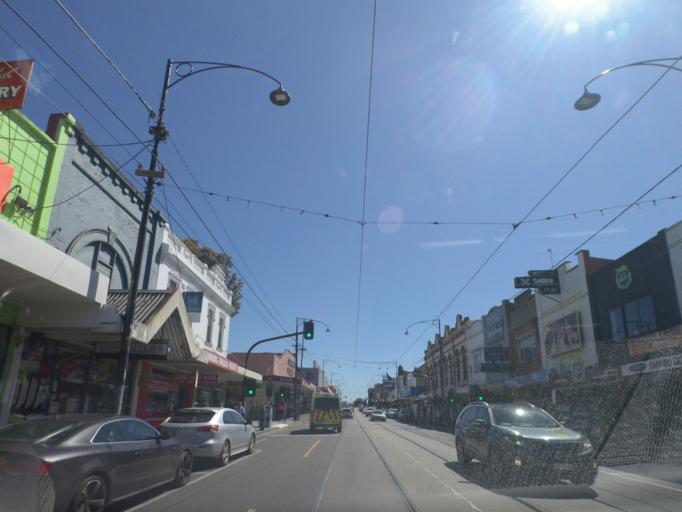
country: AU
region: Victoria
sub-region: Moreland
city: Coburg
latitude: -37.7435
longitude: 144.9661
